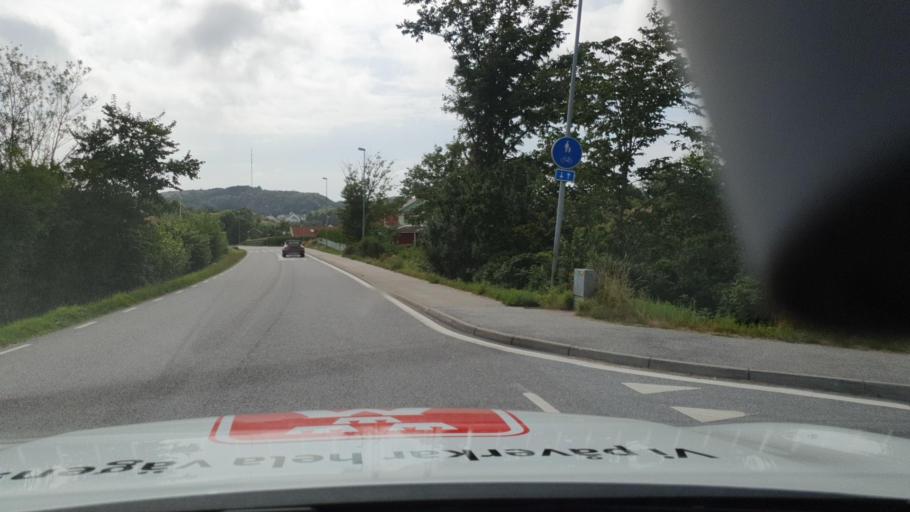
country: SE
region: Vaestra Goetaland
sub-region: Sotenas Kommun
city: Hunnebostrand
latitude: 58.5571
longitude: 11.2774
